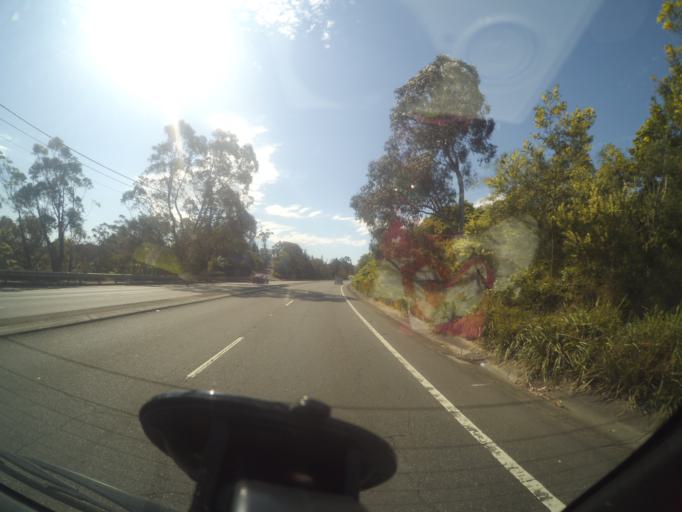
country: AU
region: New South Wales
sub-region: Blue Mountains Municipality
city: Hazelbrook
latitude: -33.7020
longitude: 150.5314
